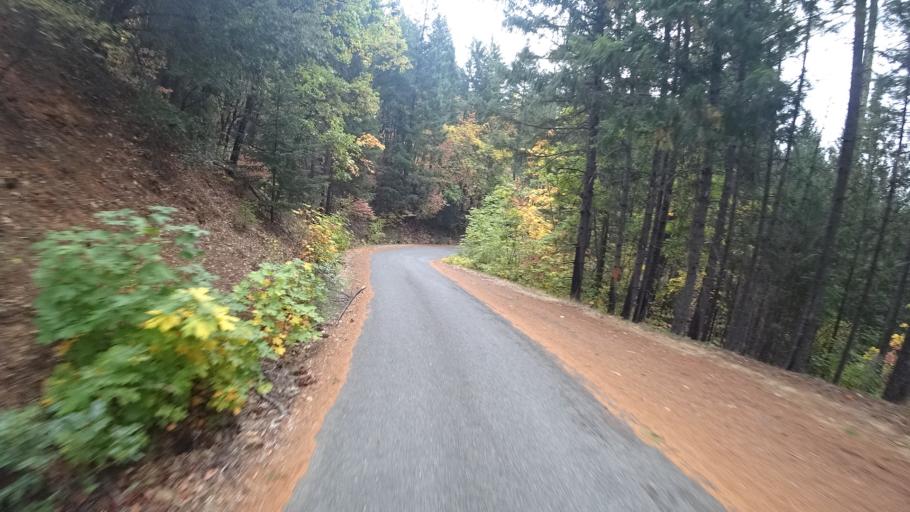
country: US
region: California
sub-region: Siskiyou County
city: Happy Camp
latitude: 41.8238
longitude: -123.3300
